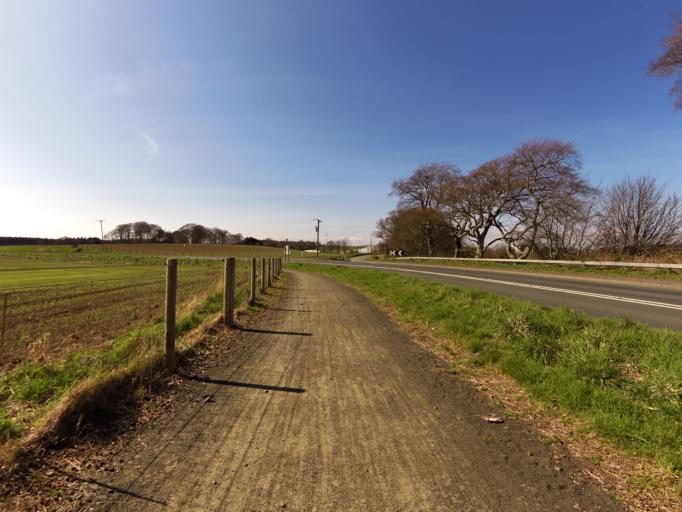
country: GB
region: Scotland
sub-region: Angus
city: Montrose
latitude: 56.7474
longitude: -2.4537
